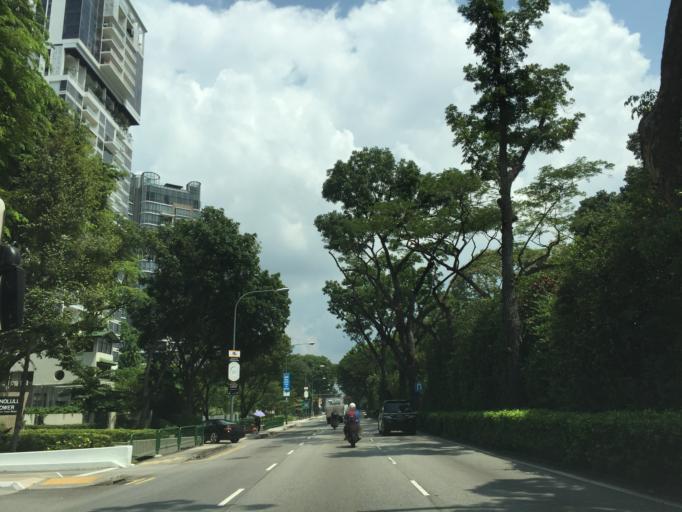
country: SG
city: Singapore
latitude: 1.3185
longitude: 103.8316
